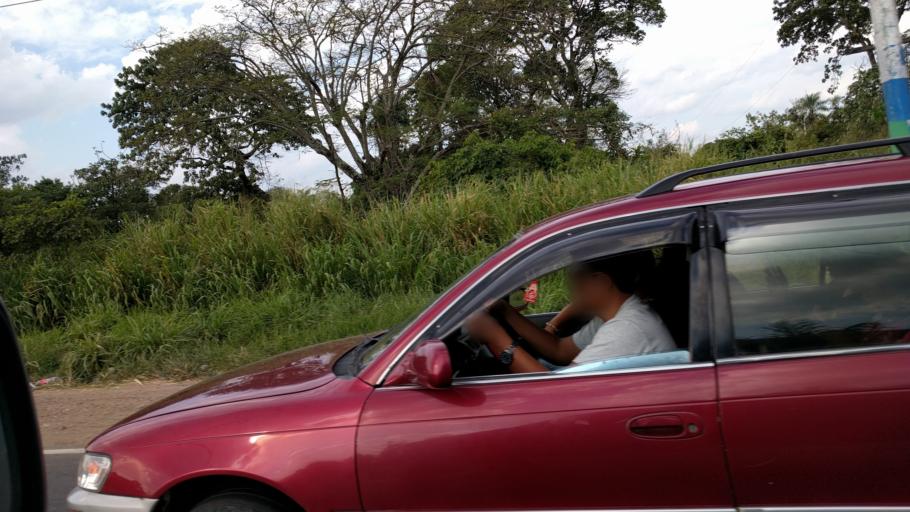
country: BO
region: Santa Cruz
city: Warnes
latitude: -17.5479
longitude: -63.1602
